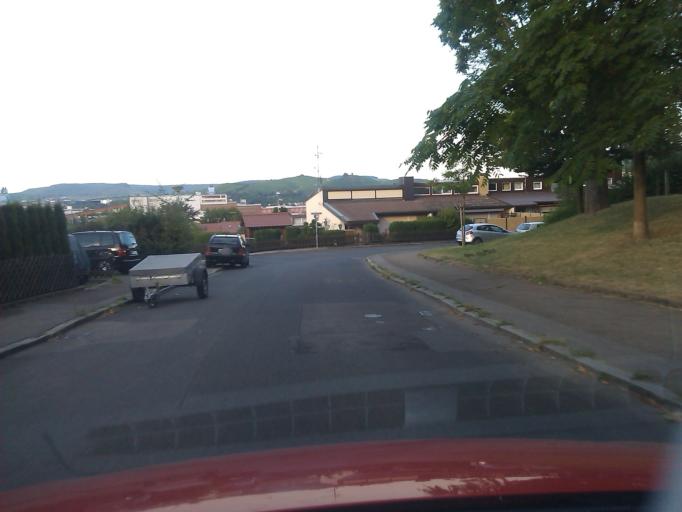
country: DE
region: Baden-Wuerttemberg
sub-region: Regierungsbezirk Stuttgart
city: Heilbronn
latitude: 49.1649
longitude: 9.2021
